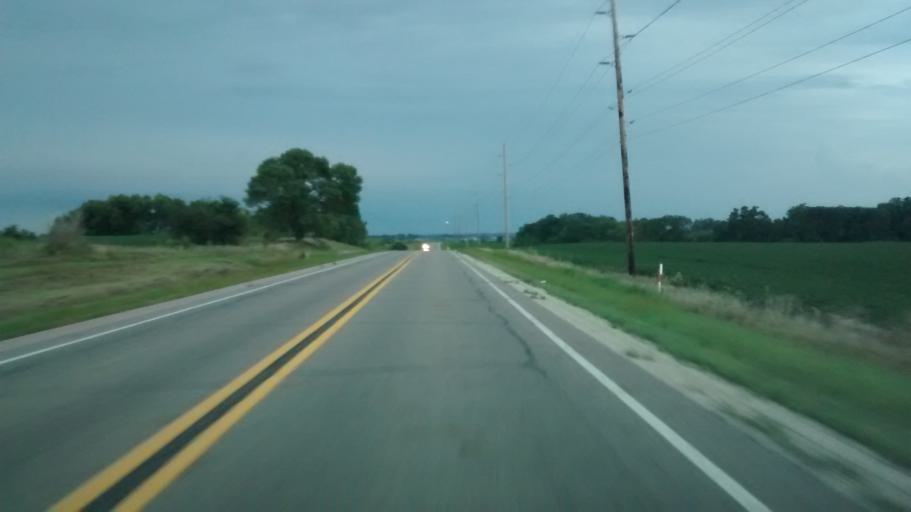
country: US
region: Iowa
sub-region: Woodbury County
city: Moville
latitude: 42.5154
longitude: -96.0507
